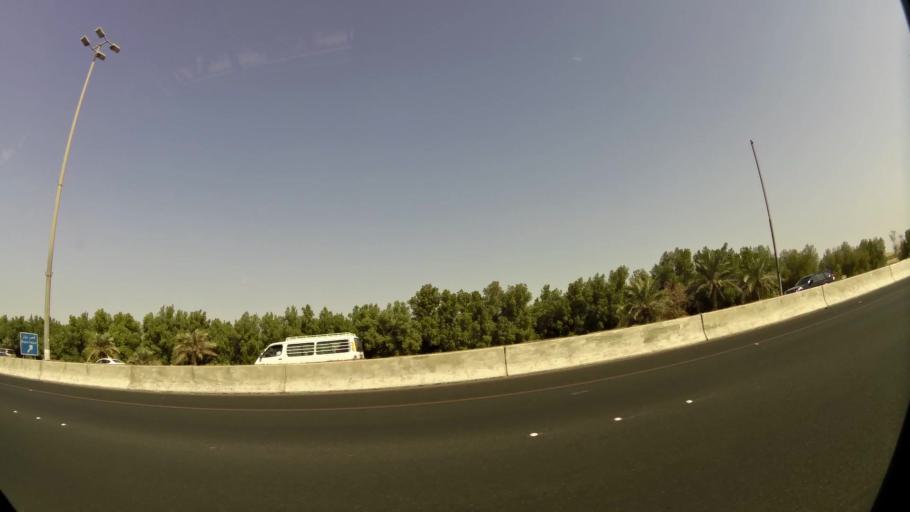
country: KW
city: Bayan
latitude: 29.2864
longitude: 48.0315
